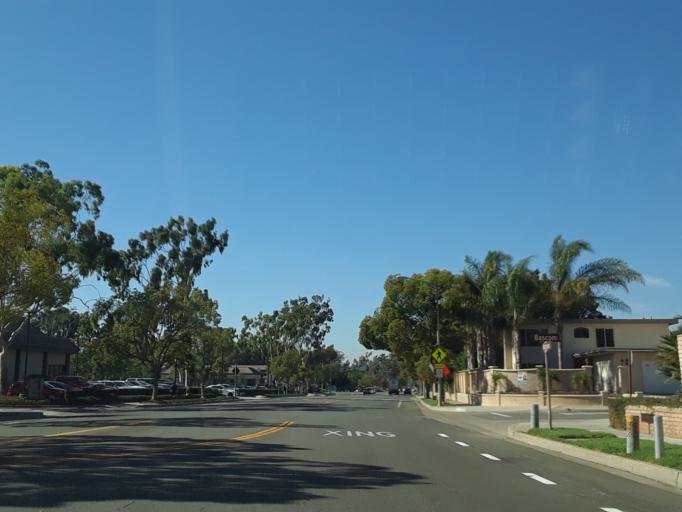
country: US
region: California
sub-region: Orange County
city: Irvine
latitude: 33.6643
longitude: -117.8242
